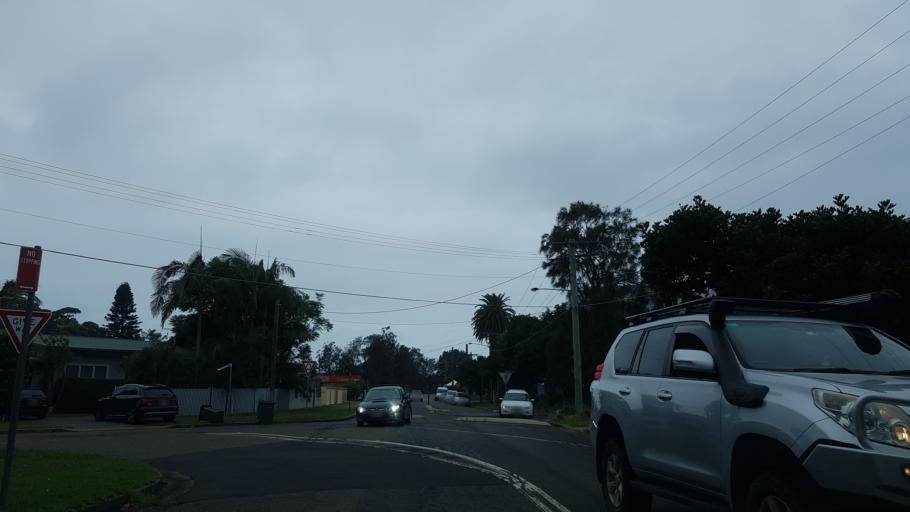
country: AU
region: New South Wales
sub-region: Pittwater
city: North Narrabeen
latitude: -33.7076
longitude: 151.2944
